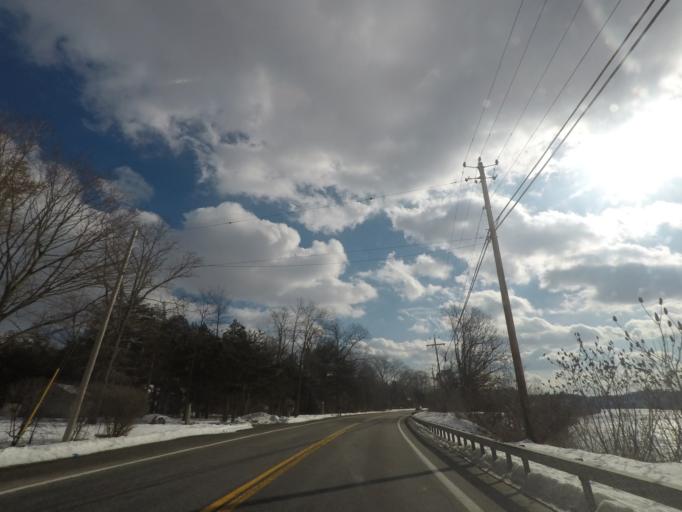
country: US
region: New York
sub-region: Schenectady County
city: East Glenville
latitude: 42.8512
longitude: -73.8795
